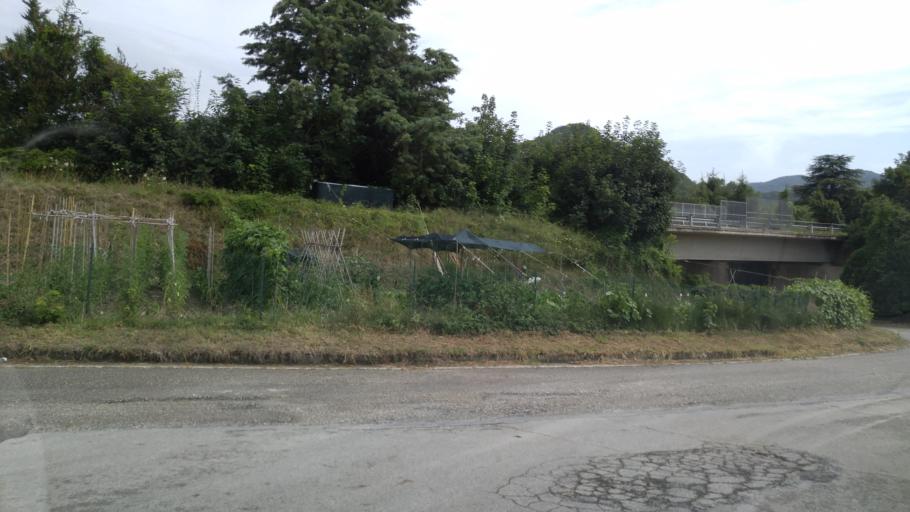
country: IT
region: The Marches
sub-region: Provincia di Pesaro e Urbino
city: Acqualagna
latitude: 43.6351
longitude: 12.6857
